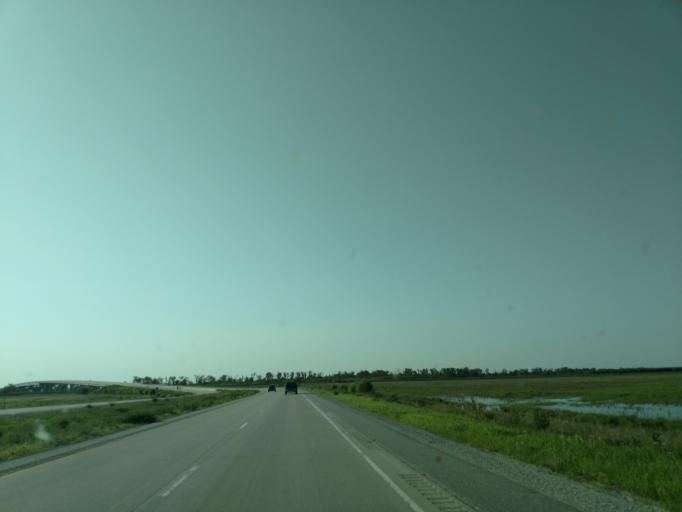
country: US
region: Nebraska
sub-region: Cass County
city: Plattsmouth
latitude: 41.0605
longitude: -95.8686
